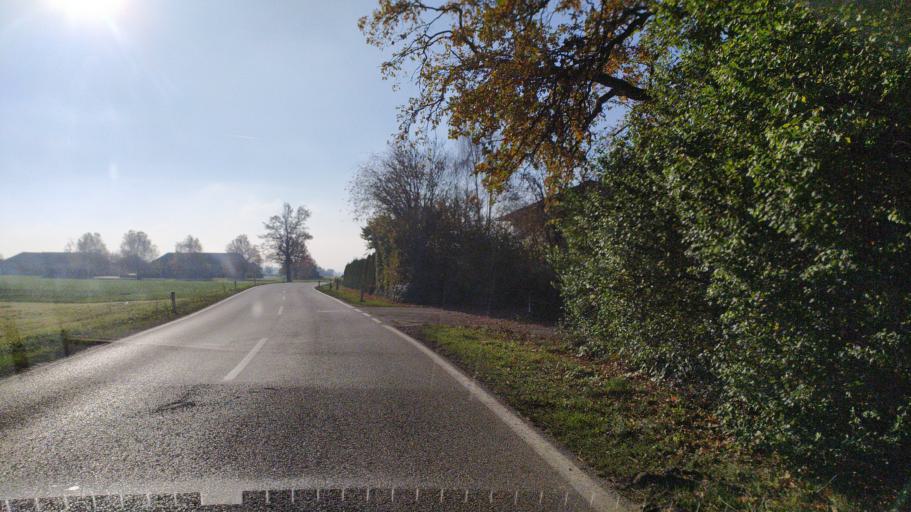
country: AT
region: Upper Austria
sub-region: Politischer Bezirk Perg
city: Perg
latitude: 48.2335
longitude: 14.6227
